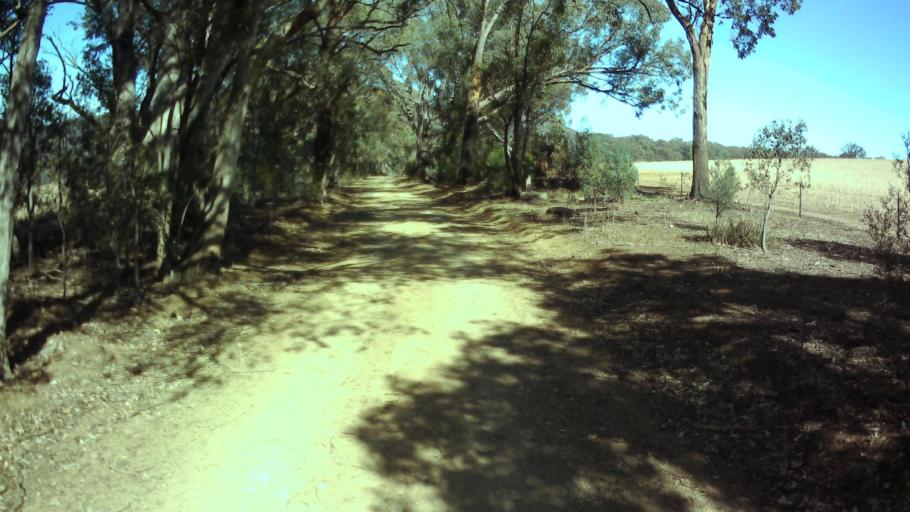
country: AU
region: New South Wales
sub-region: Weddin
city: Grenfell
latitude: -33.9004
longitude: 148.0216
